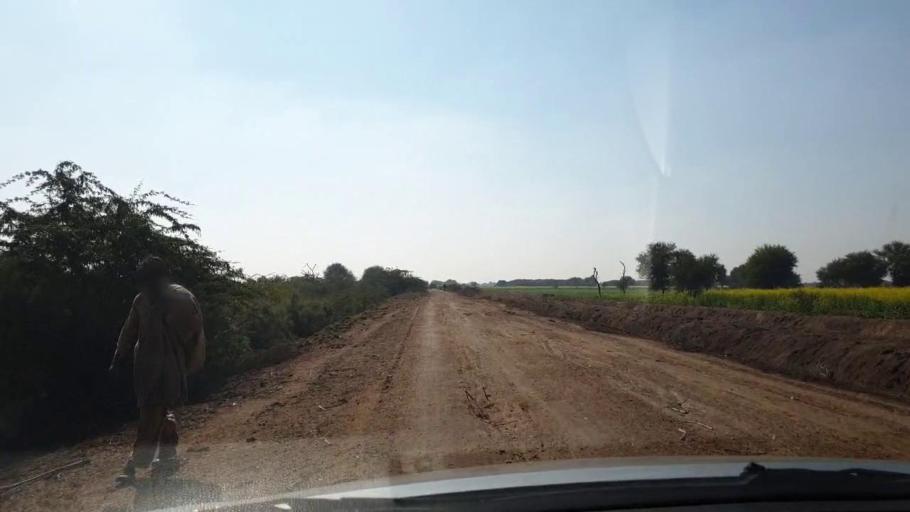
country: PK
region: Sindh
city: Jhol
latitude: 25.8688
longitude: 68.8953
